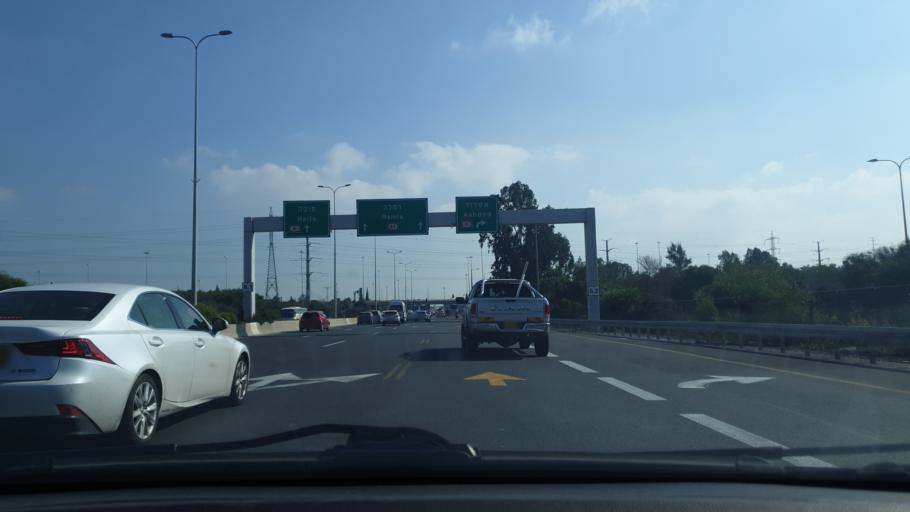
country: IL
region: Tel Aviv
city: Azor
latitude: 32.0142
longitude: 34.8116
